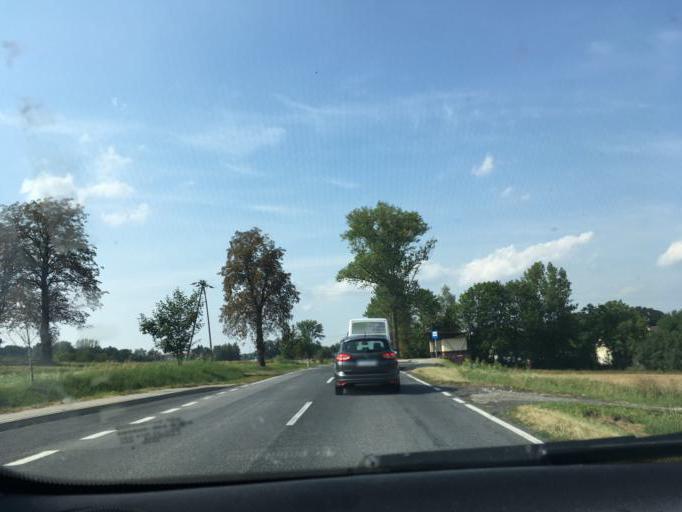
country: PL
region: Opole Voivodeship
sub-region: Powiat prudnicki
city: Laka Prudnicka
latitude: 50.3758
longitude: 17.5341
